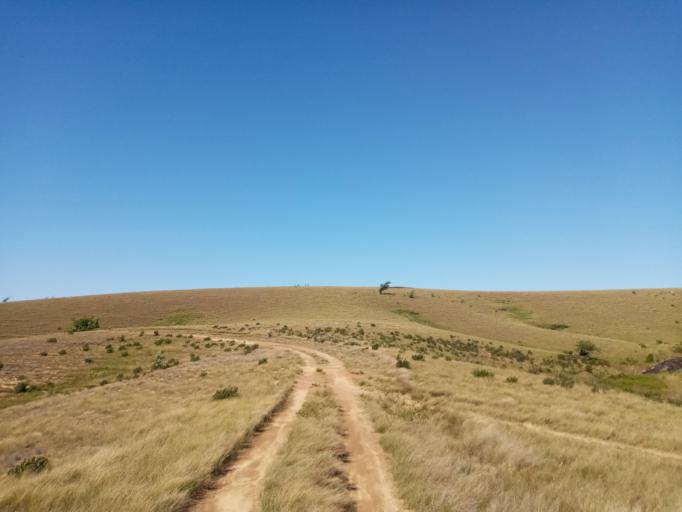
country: MG
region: Anosy
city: Fort Dauphin
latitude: -24.9099
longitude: 47.0739
